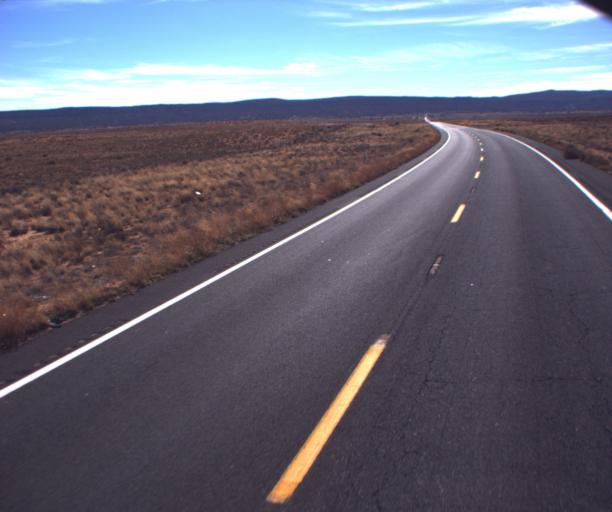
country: US
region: Arizona
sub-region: Coconino County
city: Kaibito
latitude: 36.4842
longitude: -110.7049
